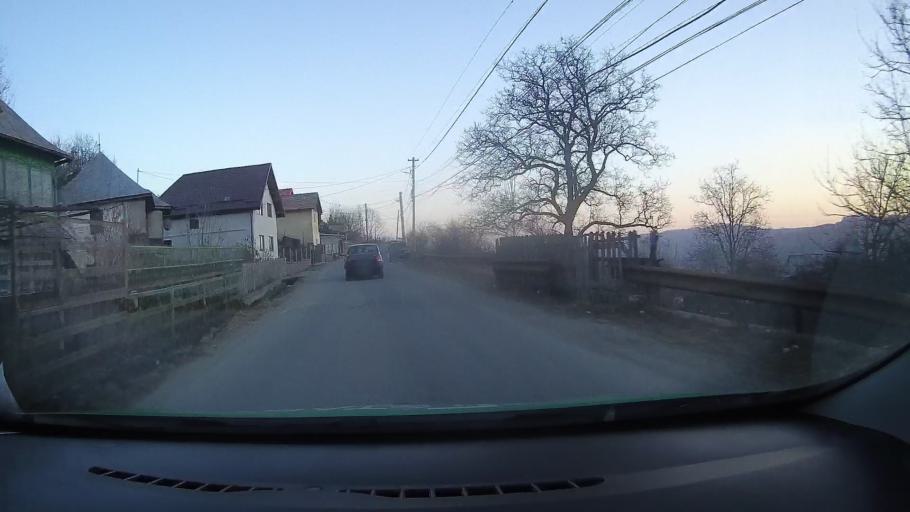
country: RO
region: Prahova
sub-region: Comuna Comarnic
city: Comarnic
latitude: 45.2474
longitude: 25.6393
